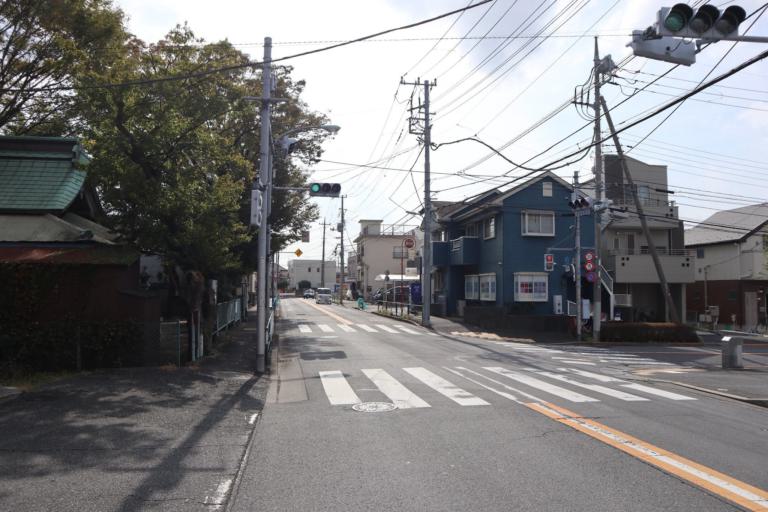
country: JP
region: Tokyo
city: Urayasu
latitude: 35.6745
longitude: 139.8846
